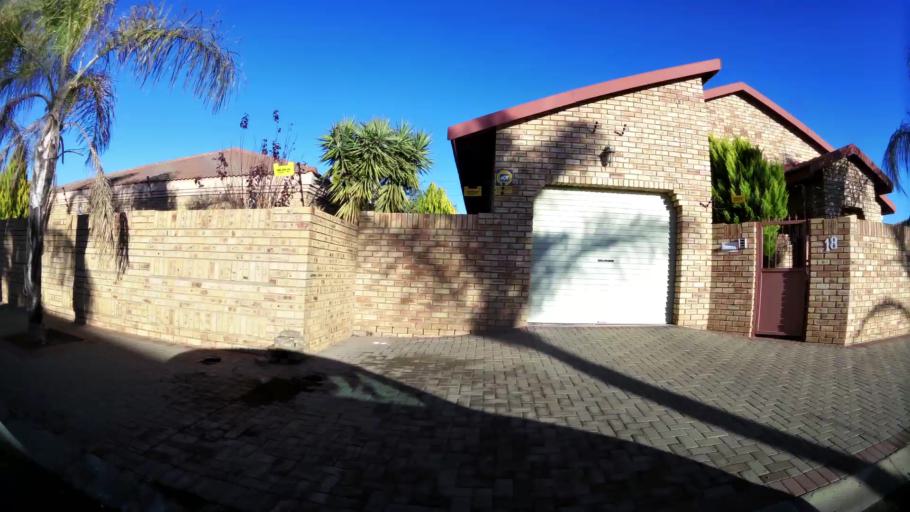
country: ZA
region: Northern Cape
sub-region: Frances Baard District Municipality
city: Kimberley
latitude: -28.7555
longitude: 24.7554
